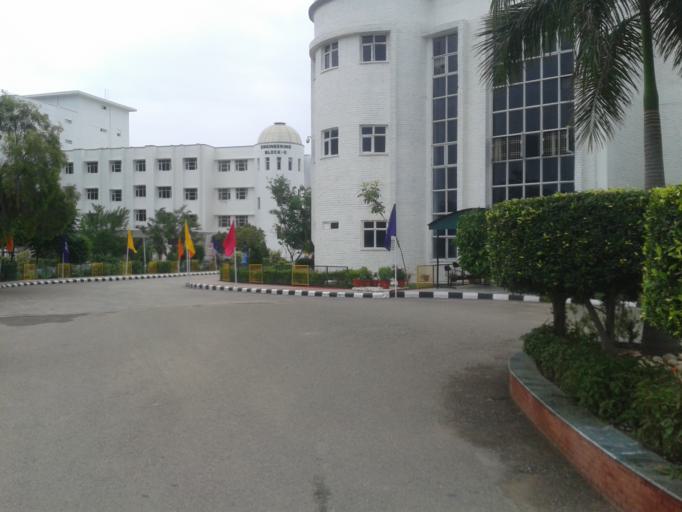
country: IN
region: Punjab
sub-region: Ajitgarh
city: Mohali
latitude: 30.6875
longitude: 76.6648
